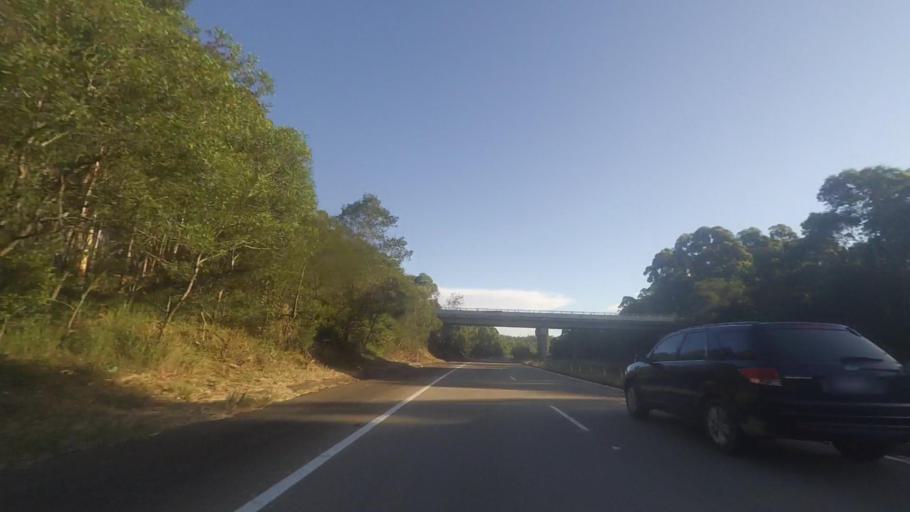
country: AU
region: New South Wales
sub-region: Great Lakes
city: Bulahdelah
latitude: -32.3008
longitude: 152.3462
